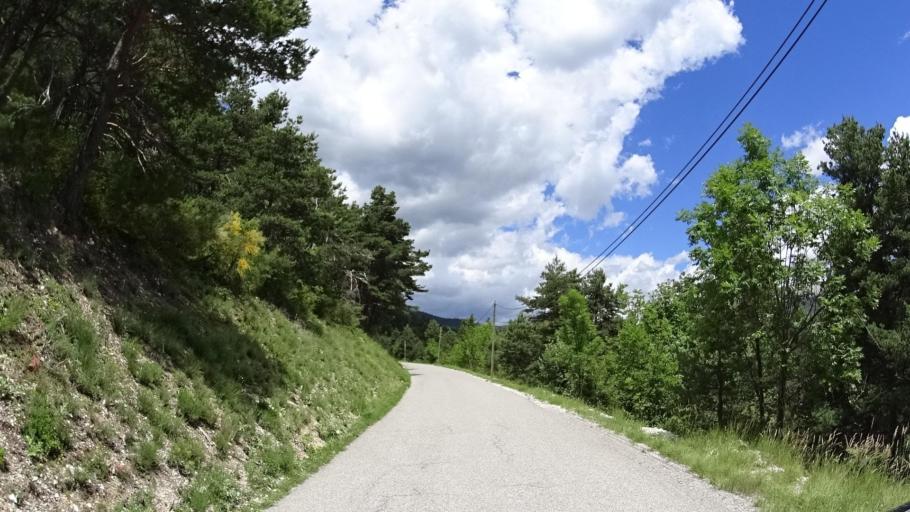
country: FR
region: Provence-Alpes-Cote d'Azur
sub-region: Departement des Alpes-de-Haute-Provence
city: Annot
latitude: 44.0194
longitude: 6.6224
